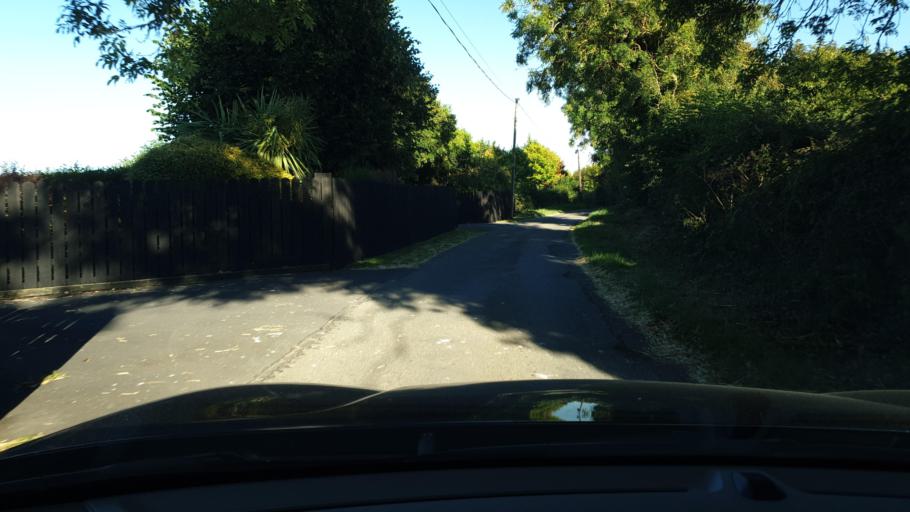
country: IE
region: Leinster
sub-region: Fingal County
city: Blanchardstown
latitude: 53.4378
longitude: -6.3630
